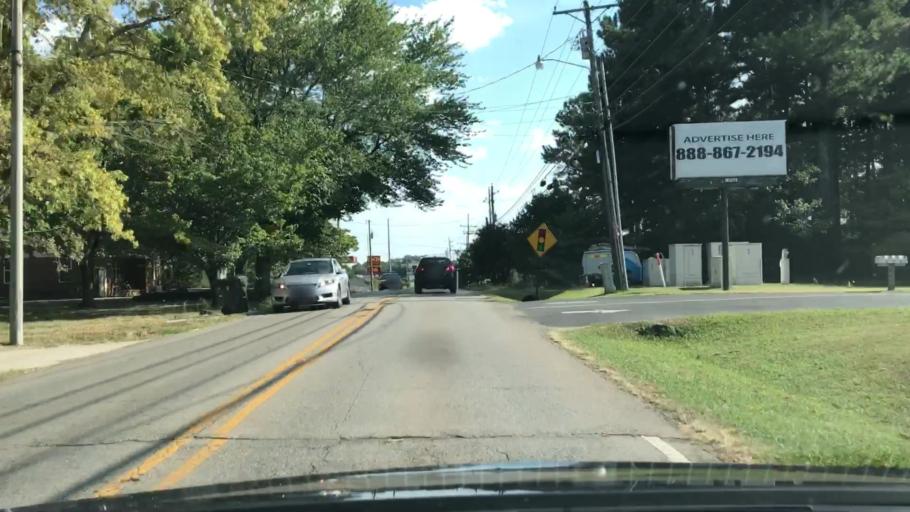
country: US
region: Alabama
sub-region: Madison County
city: Harvest
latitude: 34.8103
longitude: -86.7492
